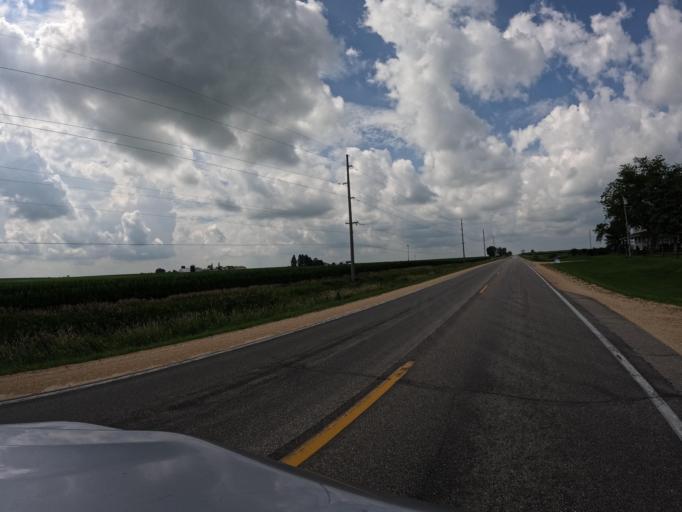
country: US
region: Iowa
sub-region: Clinton County
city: Camanche
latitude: 41.7767
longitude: -90.3549
